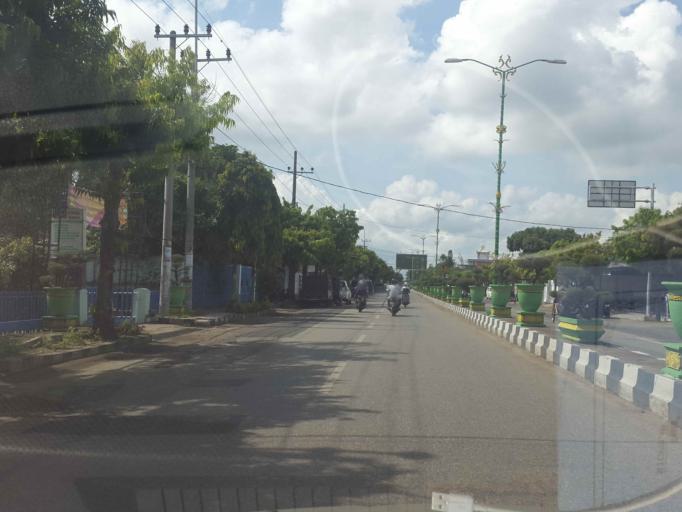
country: ID
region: East Java
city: Sumenep
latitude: -7.0141
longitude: 113.8585
